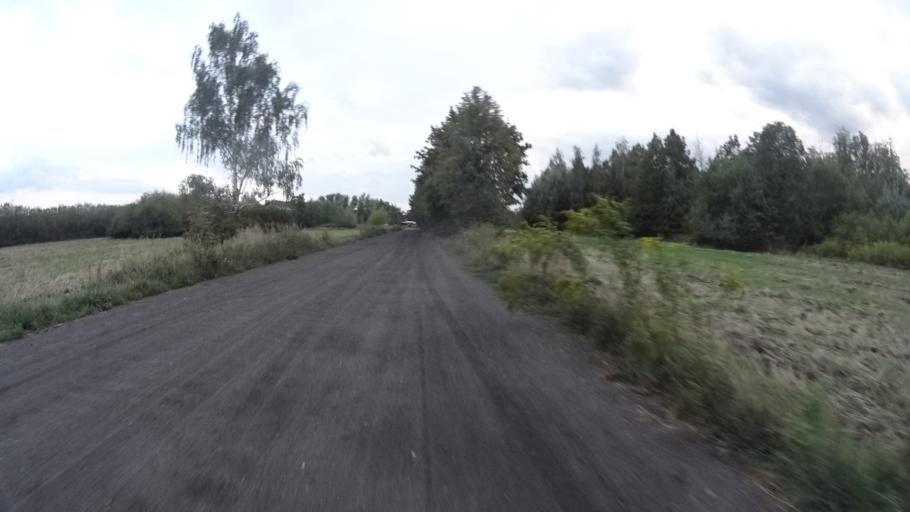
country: PL
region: Masovian Voivodeship
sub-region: Powiat warszawski zachodni
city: Ozarow Mazowiecki
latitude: 52.2335
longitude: 20.7654
